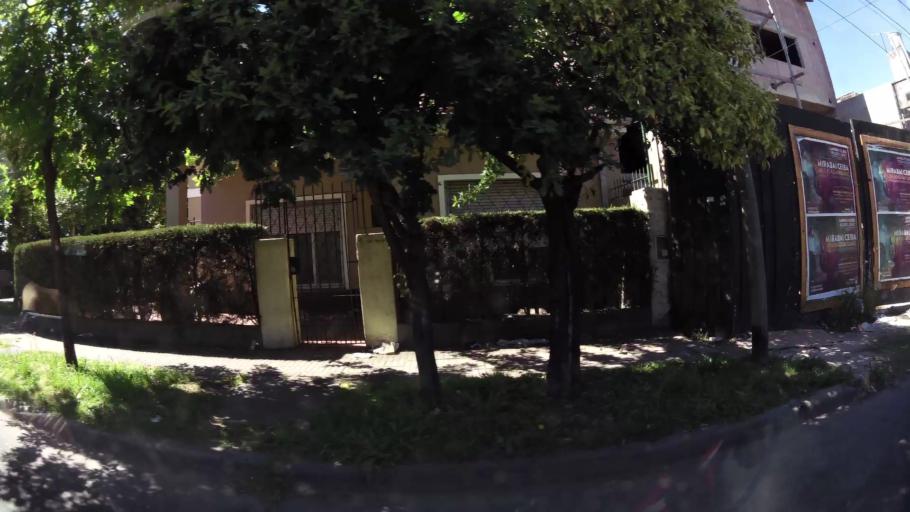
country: AR
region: Buenos Aires
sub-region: Partido de Vicente Lopez
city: Olivos
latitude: -34.5177
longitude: -58.5232
